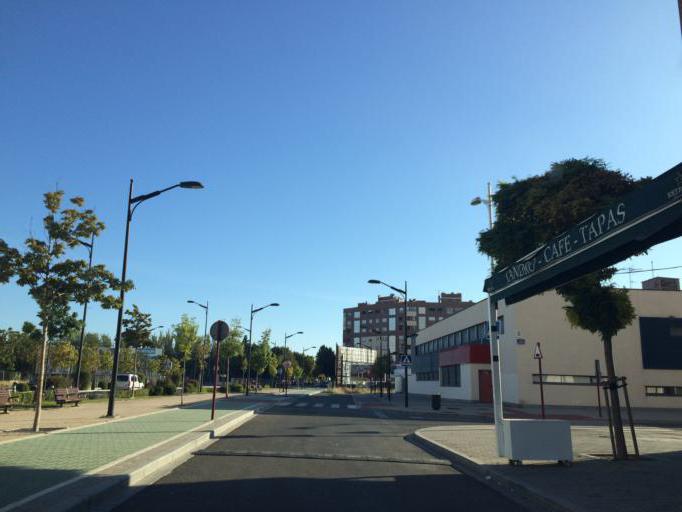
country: ES
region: Castille-La Mancha
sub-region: Provincia de Albacete
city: Albacete
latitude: 39.0057
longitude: -1.8709
